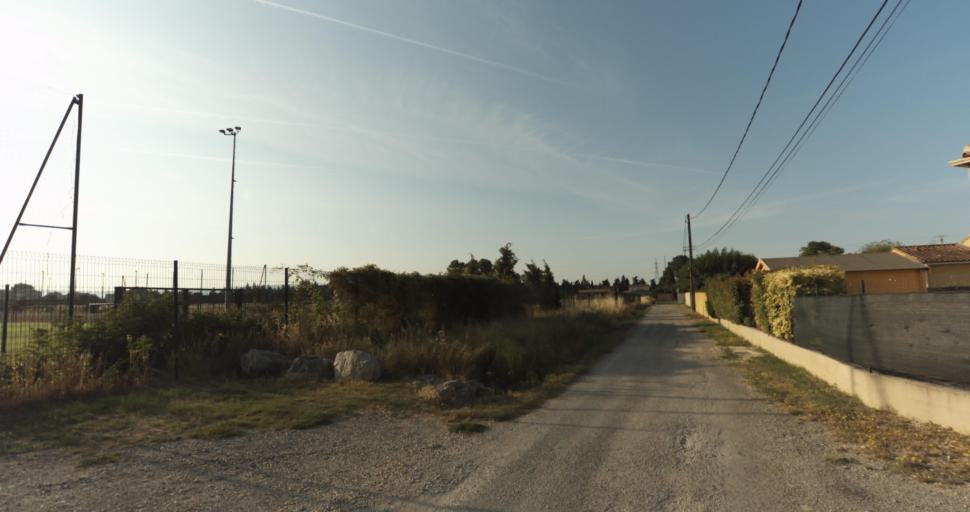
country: FR
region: Provence-Alpes-Cote d'Azur
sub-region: Departement du Vaucluse
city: Monteux
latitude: 44.0283
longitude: 5.0030
